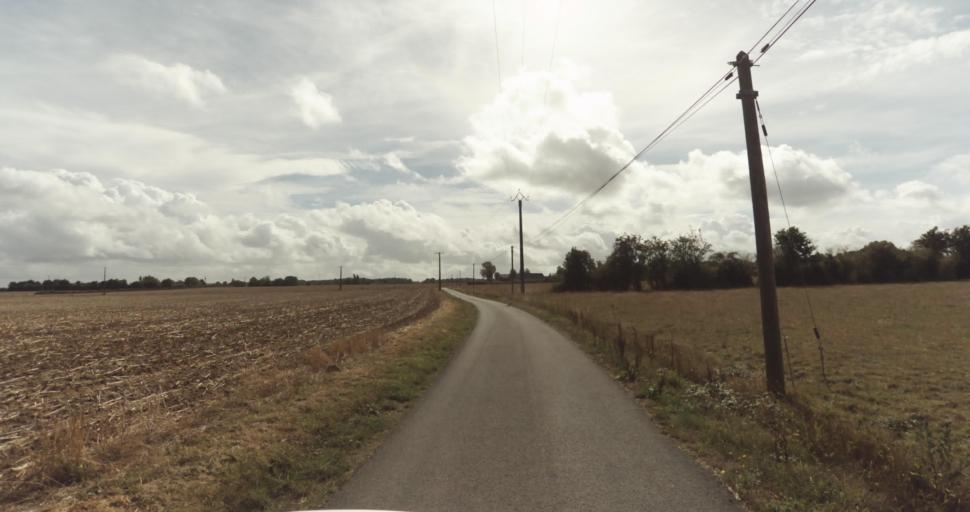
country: FR
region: Lower Normandy
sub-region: Departement de l'Orne
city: Gace
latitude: 48.8216
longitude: 0.3917
